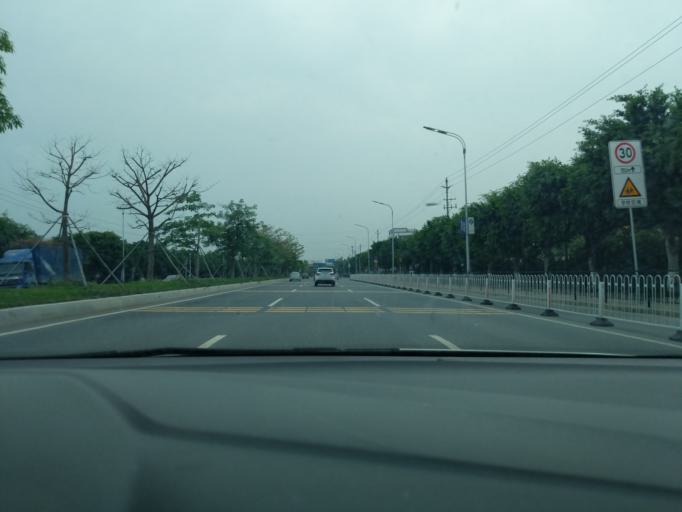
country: CN
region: Guangdong
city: Huangge
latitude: 22.8607
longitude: 113.4849
